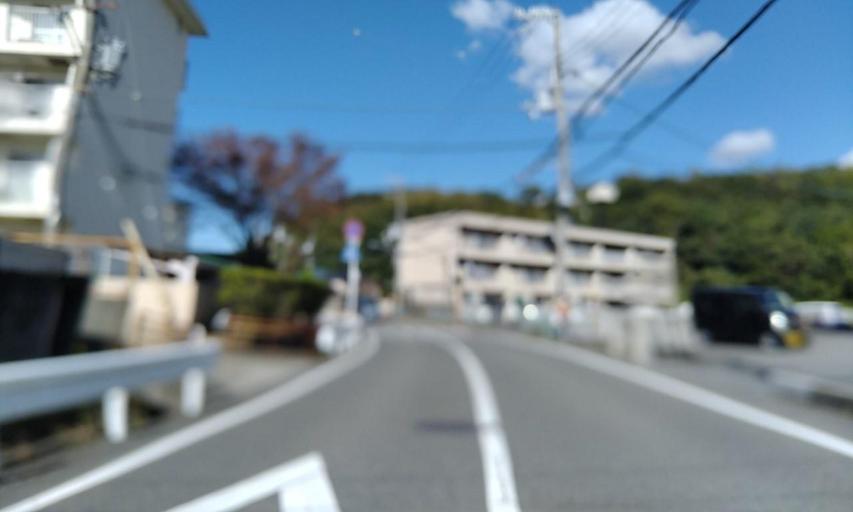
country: JP
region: Wakayama
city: Wakayama-shi
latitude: 34.1970
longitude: 135.1900
